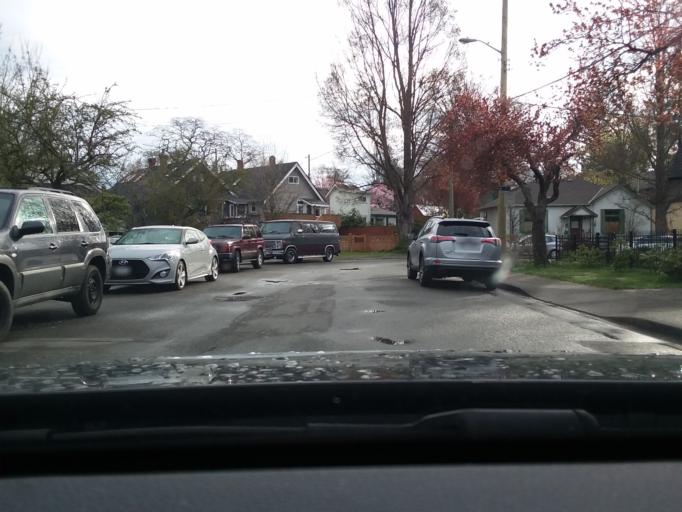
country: CA
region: British Columbia
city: Victoria
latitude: 48.4378
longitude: -123.3925
